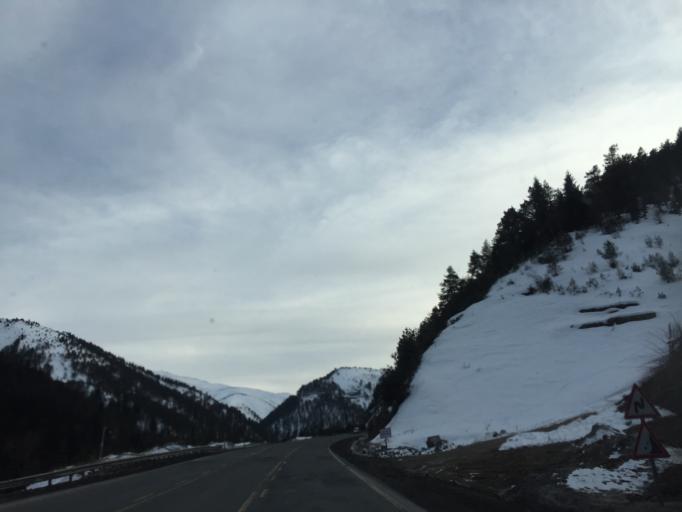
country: TR
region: Gumushane
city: Yaglidere
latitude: 40.6687
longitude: 39.4172
